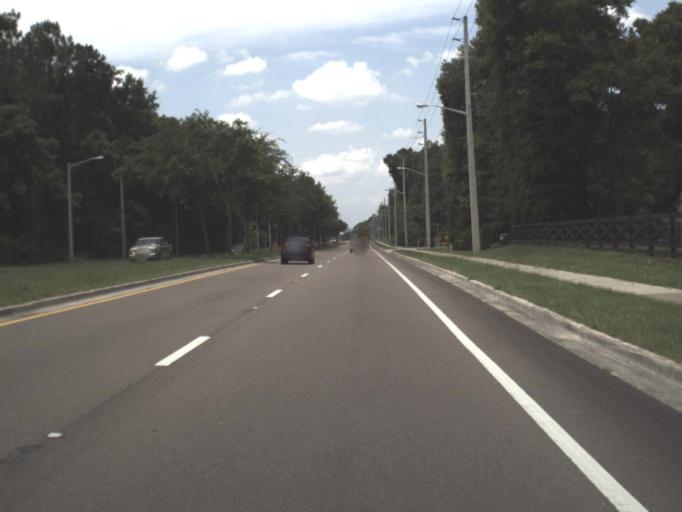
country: US
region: Florida
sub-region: Alachua County
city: Newberry
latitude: 29.6542
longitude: -82.5186
